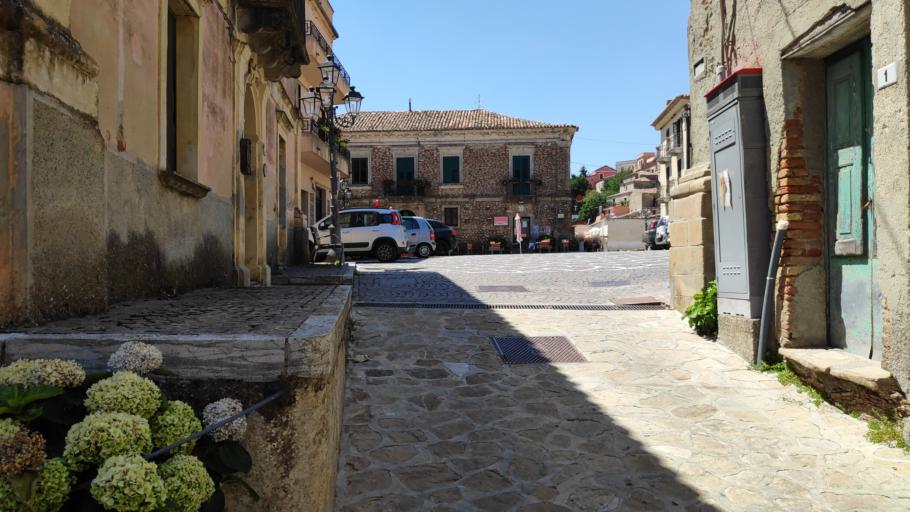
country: IT
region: Calabria
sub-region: Provincia di Reggio Calabria
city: Bova
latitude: 37.9942
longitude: 15.9333
